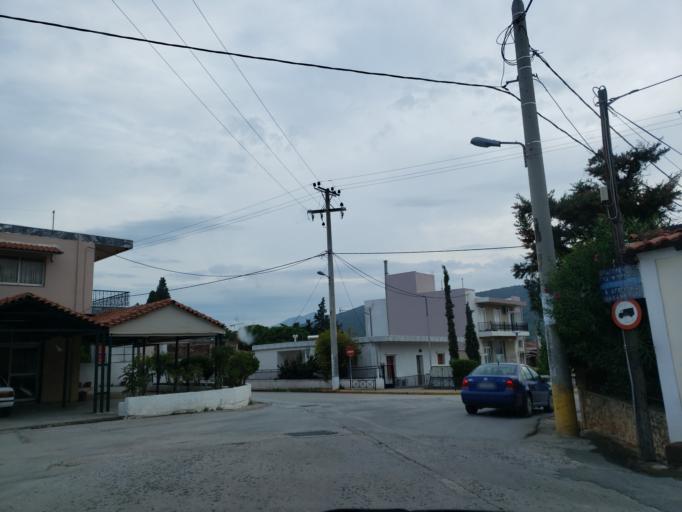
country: GR
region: Attica
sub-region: Nomarchia Anatolikis Attikis
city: Marathonas
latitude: 38.1598
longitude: 23.9611
